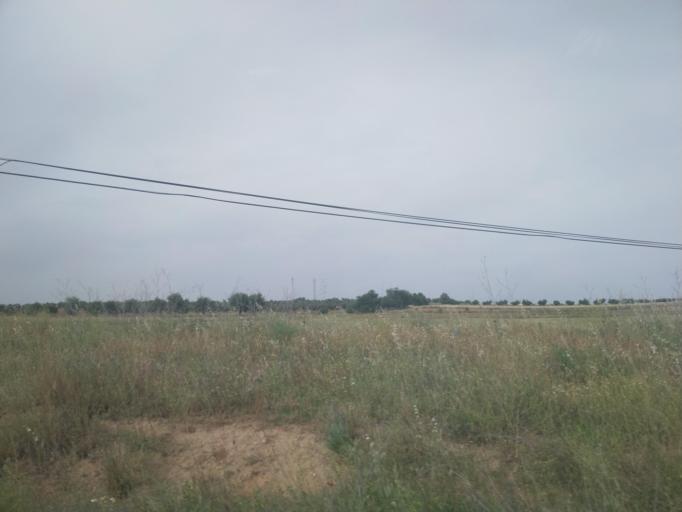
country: ES
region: Castille-La Mancha
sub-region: Province of Toledo
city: Casasbuenas
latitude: 39.7613
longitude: -4.1327
